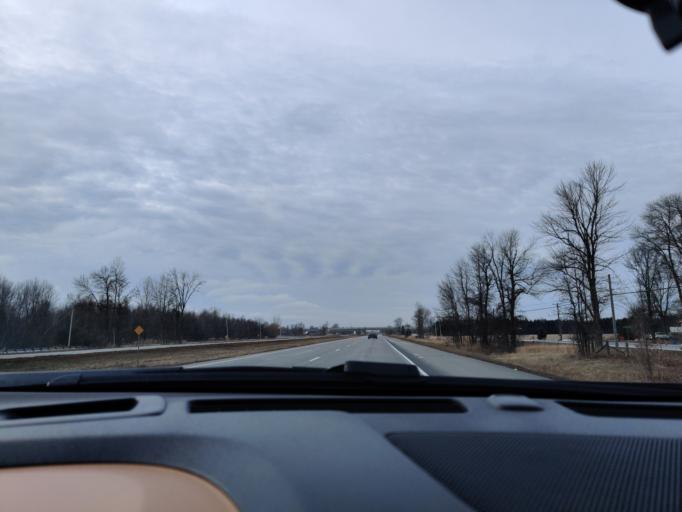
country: CA
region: Quebec
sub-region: Monteregie
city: Les Coteaux
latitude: 45.1654
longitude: -74.4377
